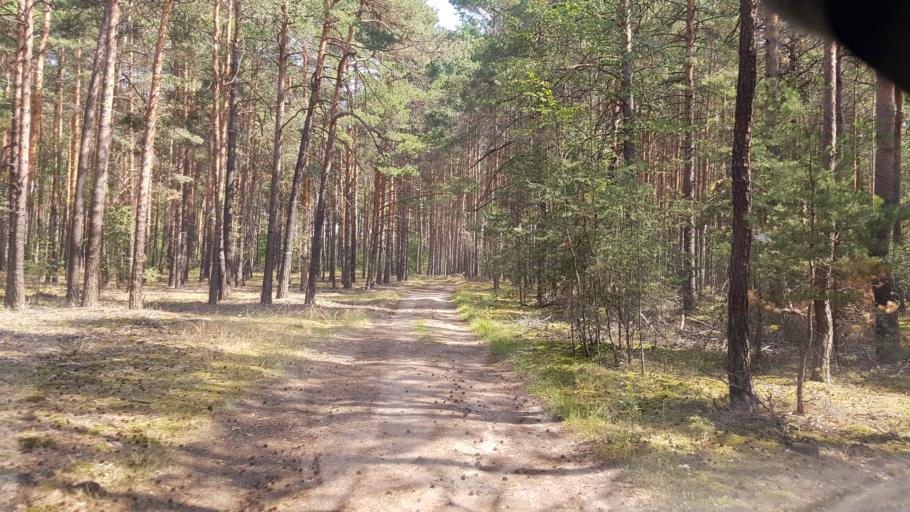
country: DE
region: Brandenburg
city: Cottbus
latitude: 51.7040
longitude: 14.4150
